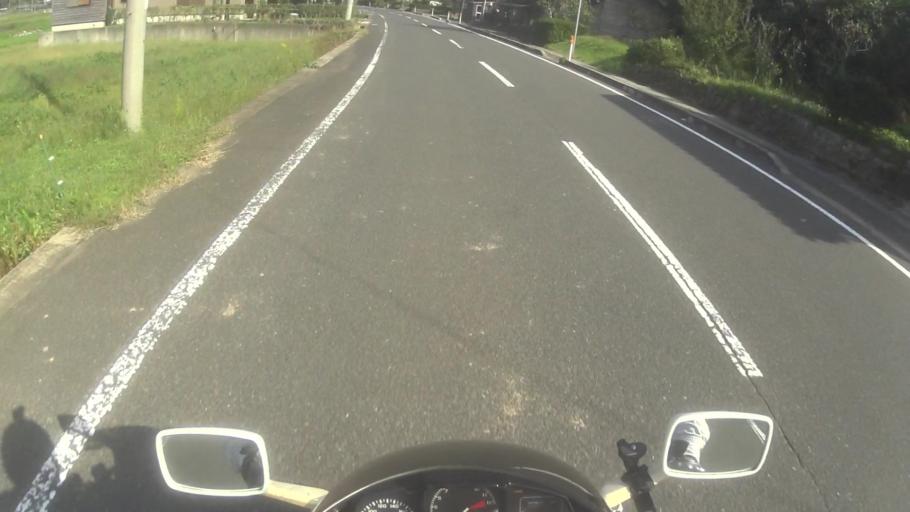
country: JP
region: Kyoto
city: Miyazu
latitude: 35.7131
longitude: 135.1104
